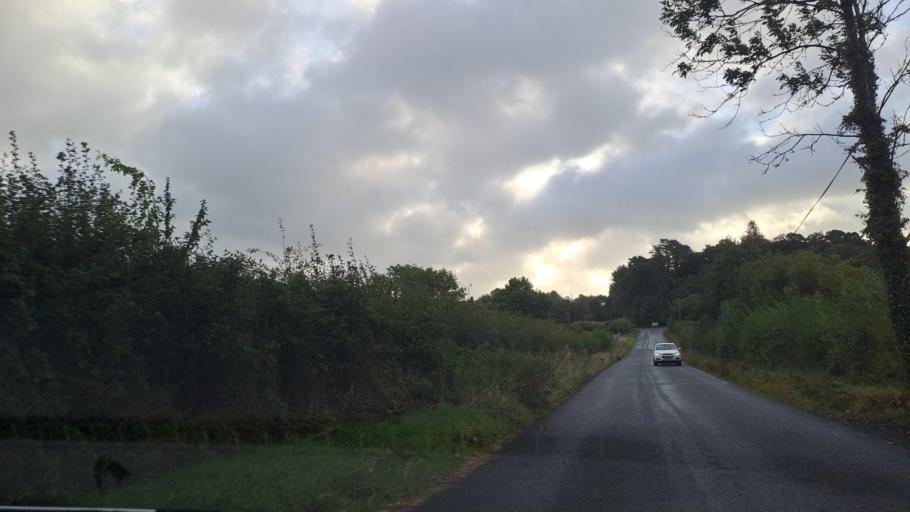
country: IE
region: Ulster
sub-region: An Cabhan
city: Kingscourt
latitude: 53.9480
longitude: -6.7680
